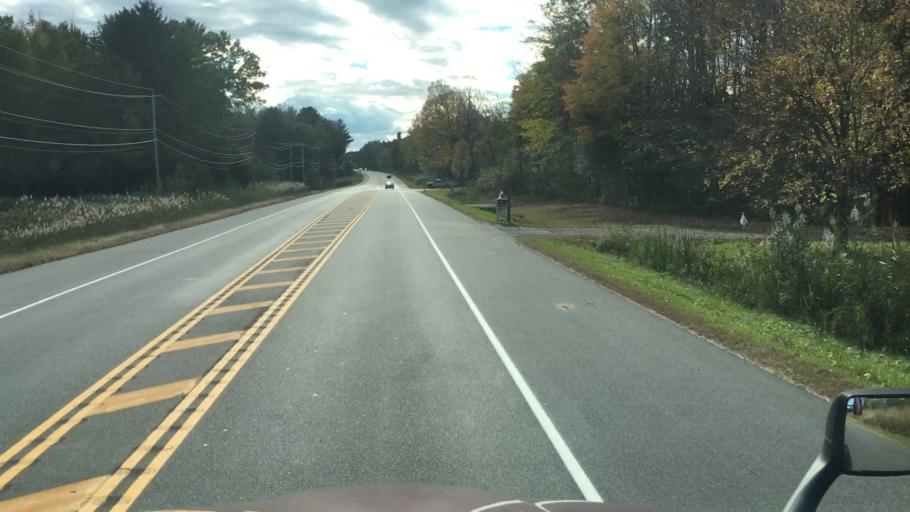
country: US
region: New York
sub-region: Saratoga County
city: Milton
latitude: 43.0353
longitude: -73.8261
